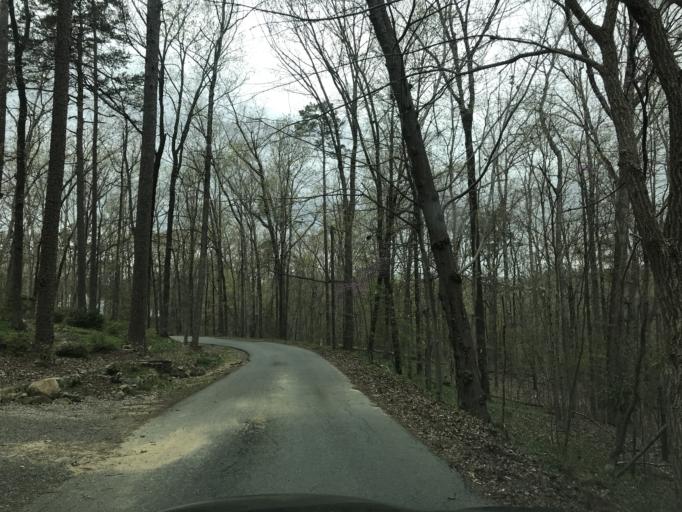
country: US
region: North Carolina
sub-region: Orange County
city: Chapel Hill
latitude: 35.9136
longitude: -79.0371
